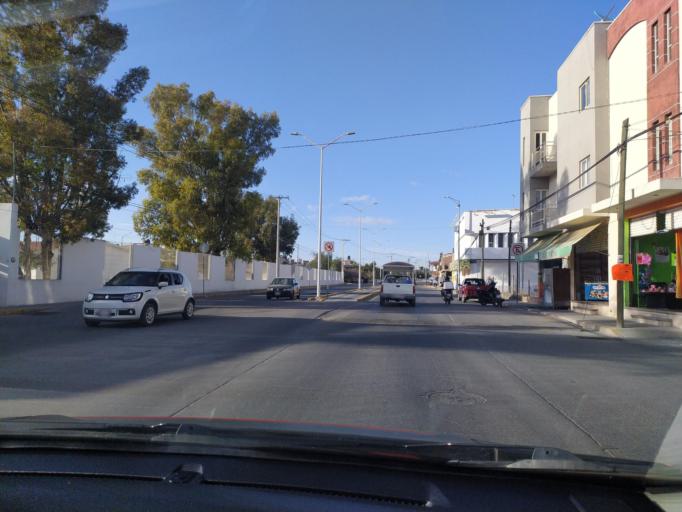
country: MX
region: Guanajuato
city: San Francisco del Rincon
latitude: 21.0193
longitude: -101.8765
